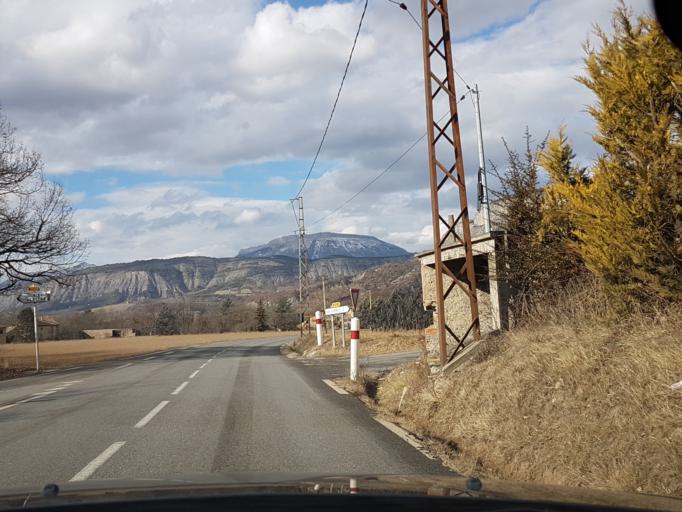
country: FR
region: Provence-Alpes-Cote d'Azur
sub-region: Departement des Hautes-Alpes
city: Tallard
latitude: 44.4767
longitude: 6.1101
